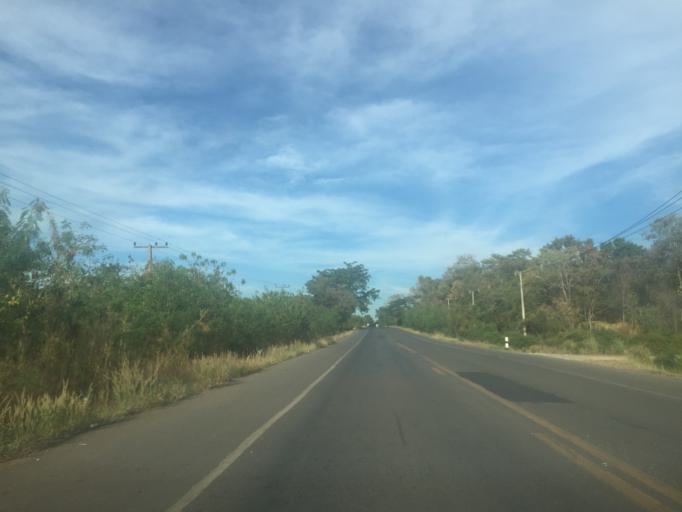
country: TH
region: Changwat Udon Thani
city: Si That
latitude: 16.9694
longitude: 103.2391
